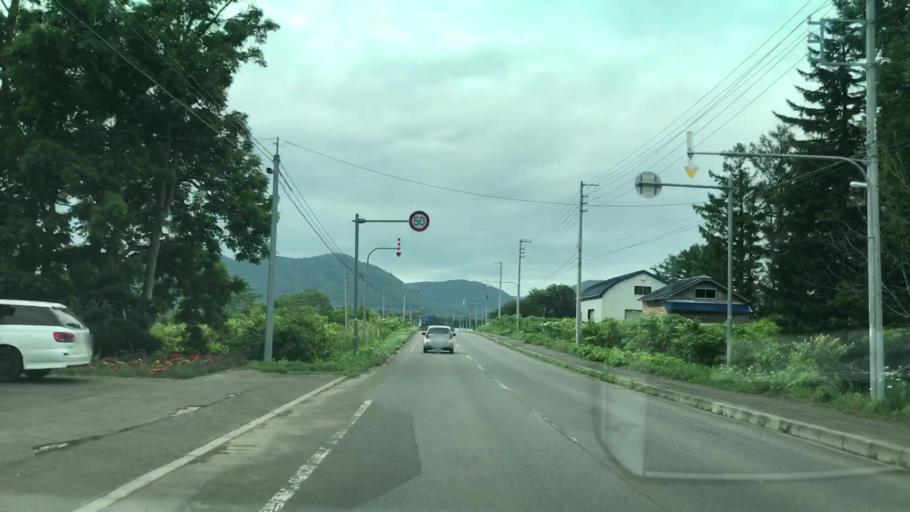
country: JP
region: Hokkaido
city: Yoichi
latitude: 43.0958
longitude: 140.8210
